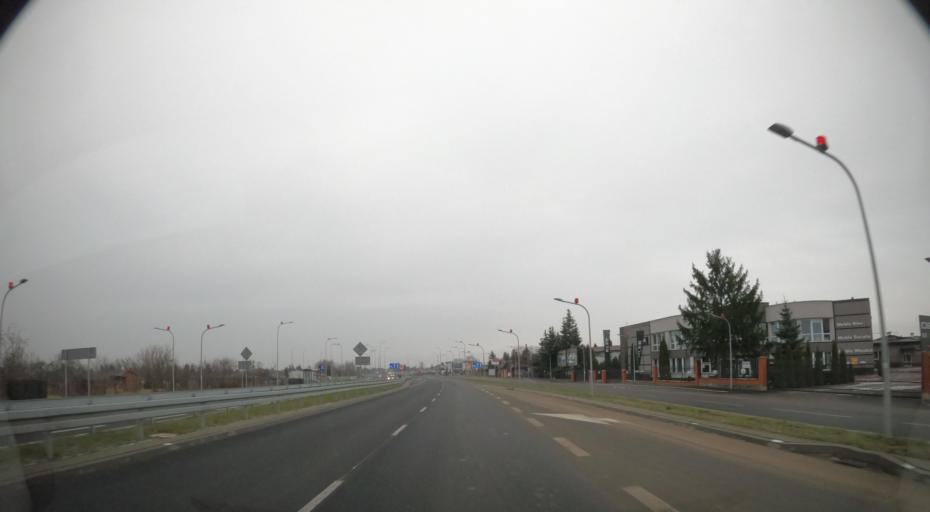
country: PL
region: Masovian Voivodeship
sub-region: Radom
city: Radom
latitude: 51.3873
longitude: 21.1908
